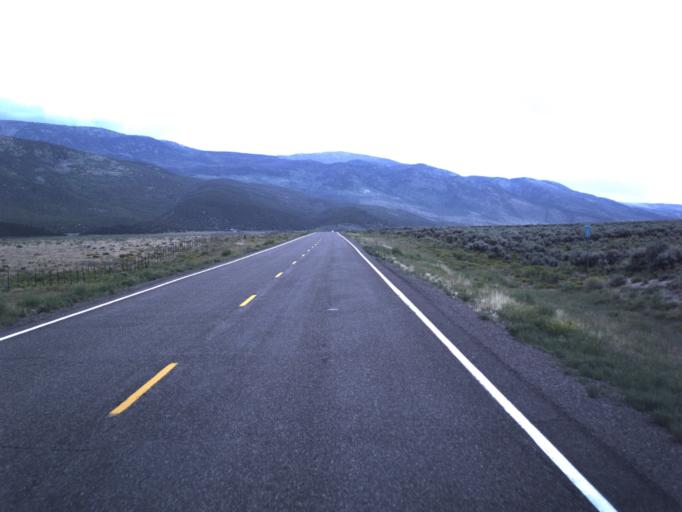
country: US
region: Utah
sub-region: Sevier County
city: Richfield
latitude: 38.6704
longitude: -111.8388
